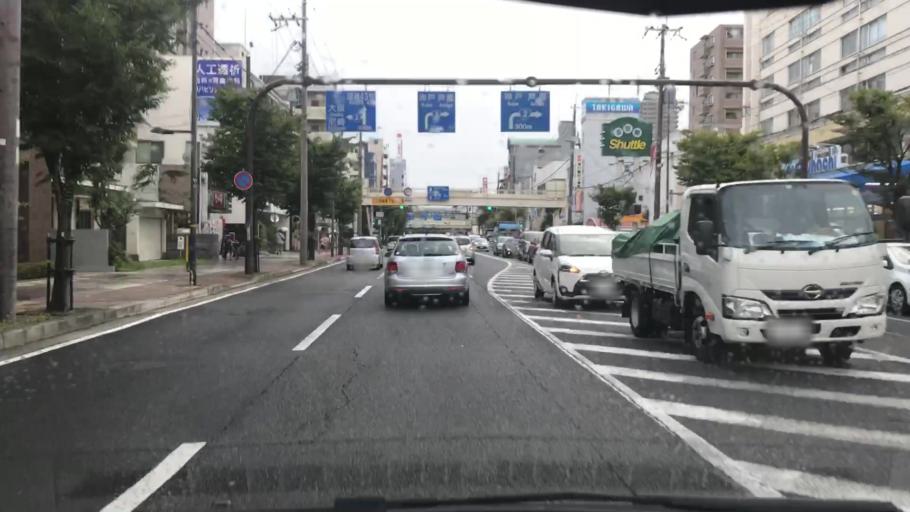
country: JP
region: Hyogo
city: Nishinomiya-hama
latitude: 34.7413
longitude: 135.3393
